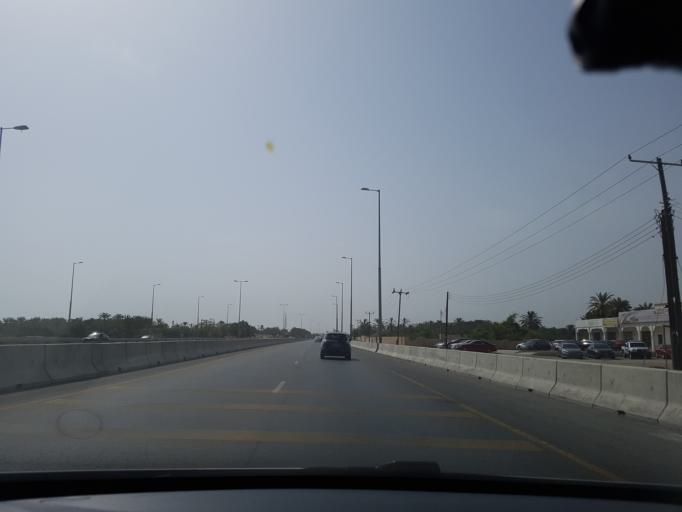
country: OM
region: Al Batinah
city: Al Khaburah
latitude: 23.9821
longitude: 57.0809
